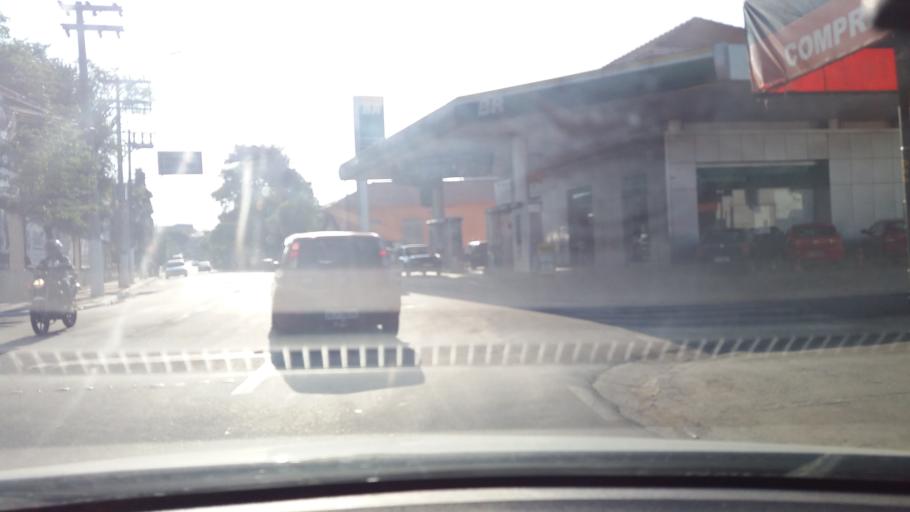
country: BR
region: Sao Paulo
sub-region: Mairipora
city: Mairipora
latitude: -23.3185
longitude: -46.5879
